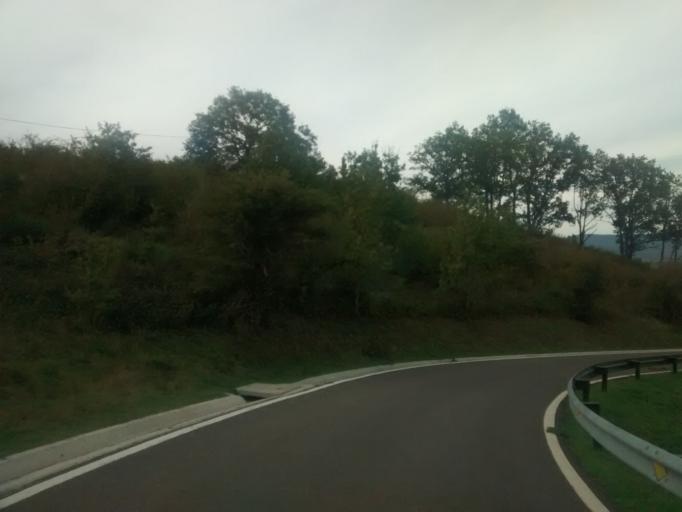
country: ES
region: Cantabria
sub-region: Provincia de Cantabria
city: San Miguel de Aguayo
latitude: 42.9683
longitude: -4.0461
